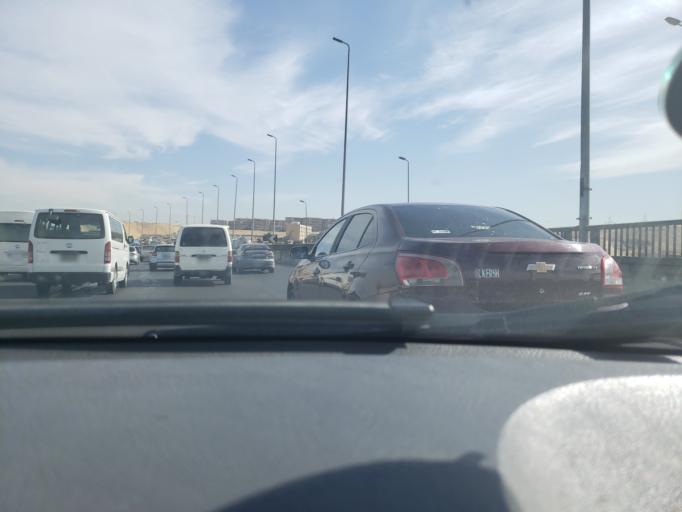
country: EG
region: Al Jizah
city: Al Jizah
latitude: 29.9960
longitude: 31.1075
